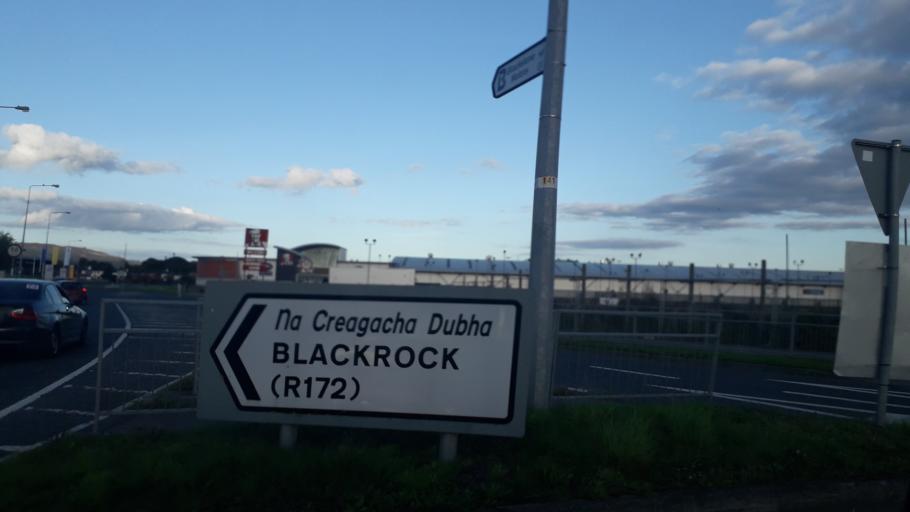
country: IE
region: Leinster
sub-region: Lu
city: Blackrock
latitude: 53.9875
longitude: -6.3787
